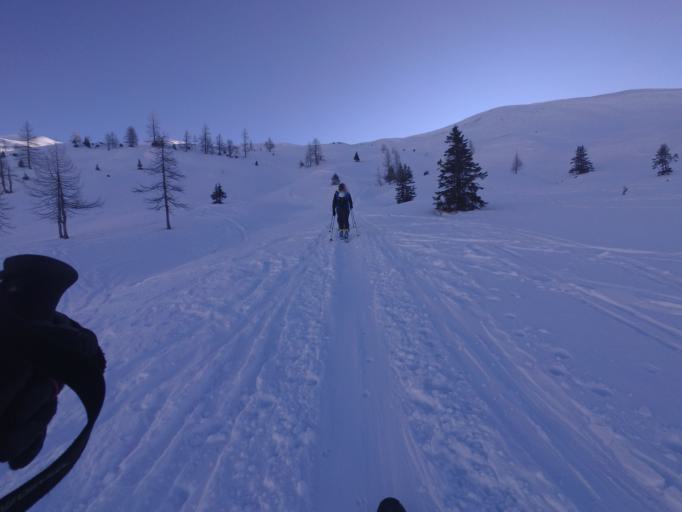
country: AT
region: Salzburg
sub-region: Politischer Bezirk Sankt Johann im Pongau
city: Huttschlag
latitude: 47.1767
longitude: 13.2983
